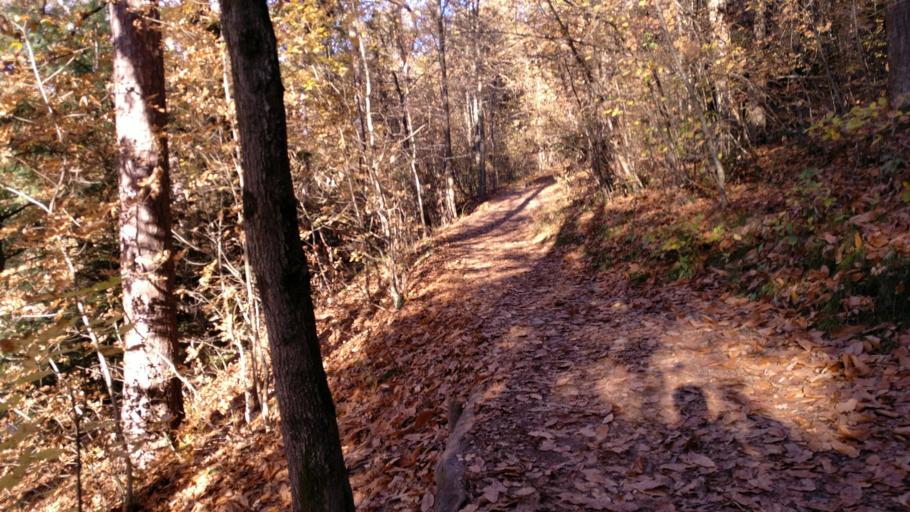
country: IT
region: Trentino-Alto Adige
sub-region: Bolzano
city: Vadena
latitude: 46.4291
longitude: 11.2975
